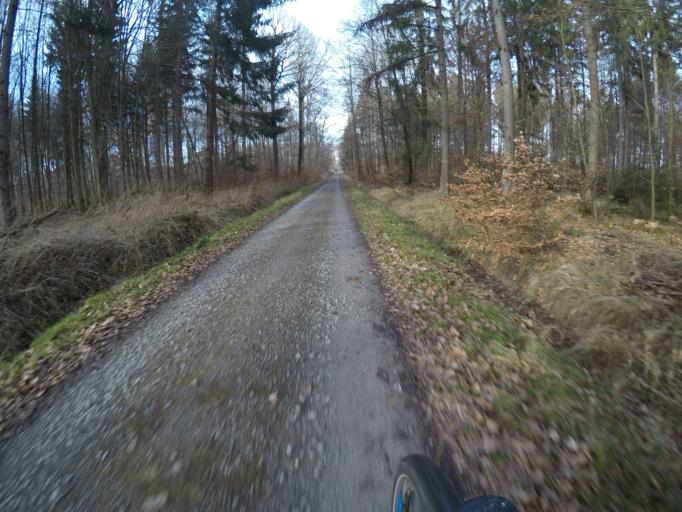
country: DE
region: Baden-Wuerttemberg
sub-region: Regierungsbezirk Stuttgart
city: Hildrizhausen
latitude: 48.6100
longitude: 8.9333
